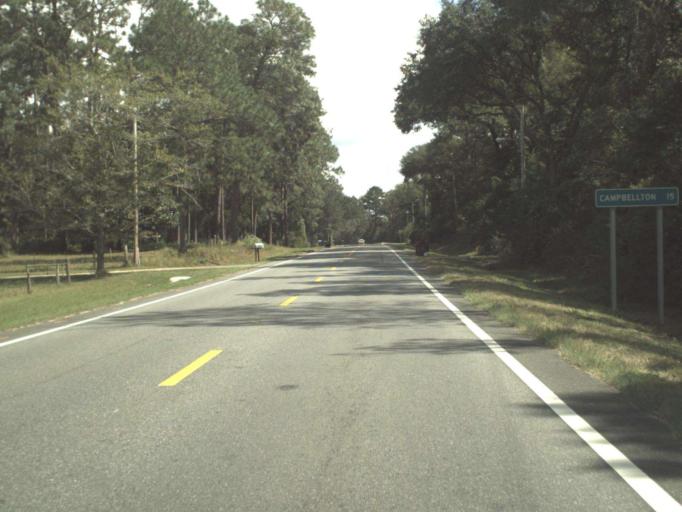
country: US
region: Florida
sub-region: Washington County
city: Chipley
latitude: 30.7899
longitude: -85.5359
